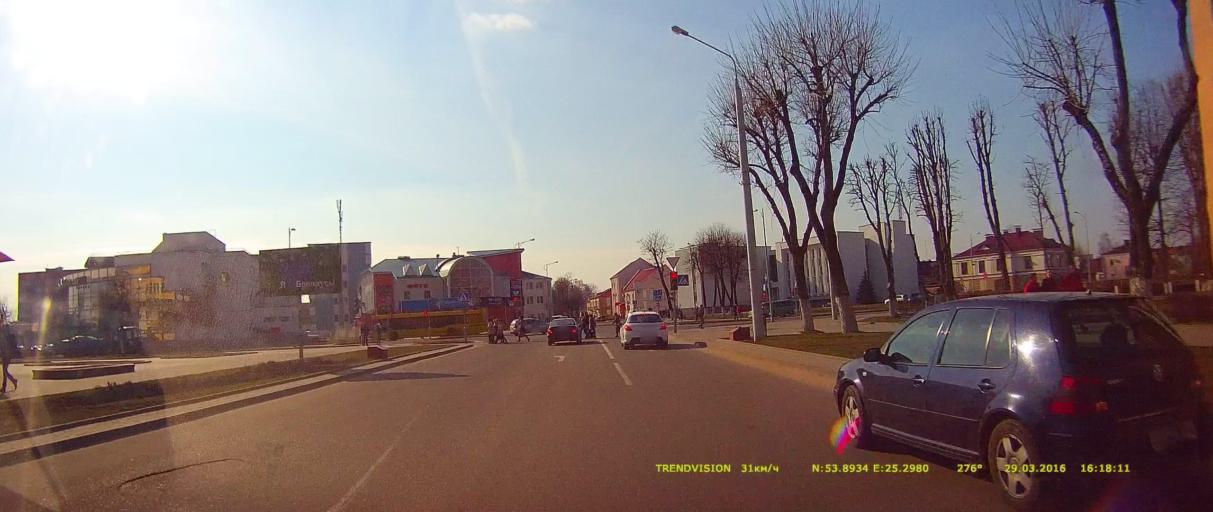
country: BY
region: Grodnenskaya
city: Lida
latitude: 53.8934
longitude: 25.2979
